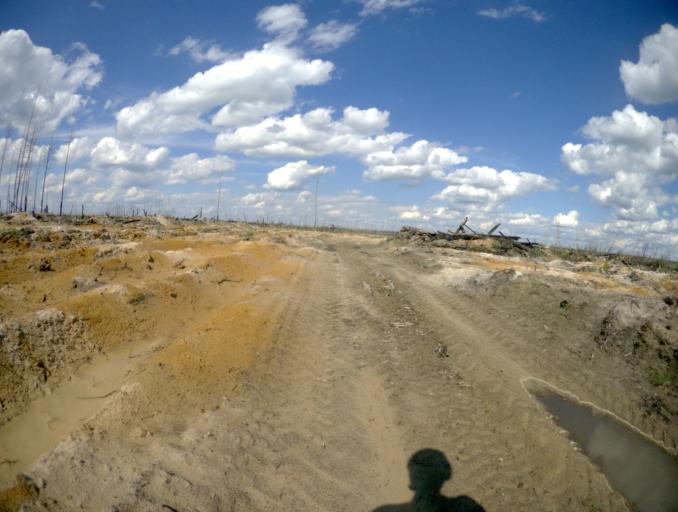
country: RU
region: Vladimir
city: Velikodvorskiy
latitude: 55.3070
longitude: 40.9048
